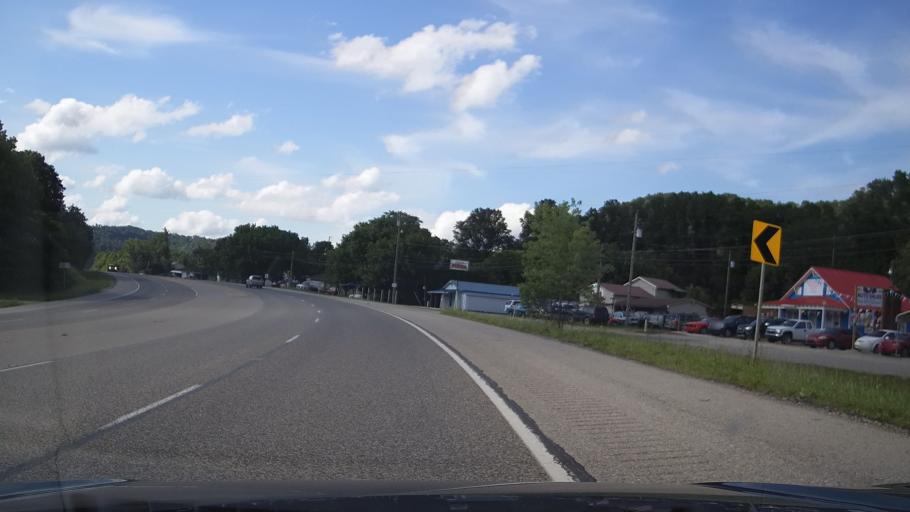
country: US
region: Kentucky
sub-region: Lawrence County
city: Louisa
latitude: 37.9942
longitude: -82.6585
